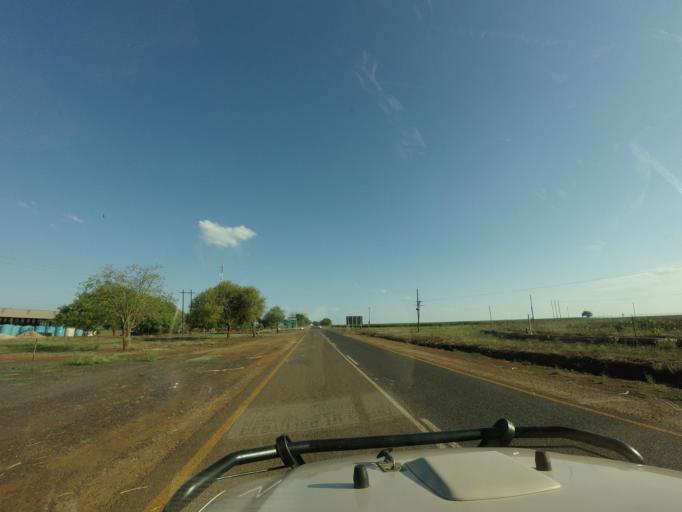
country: ZA
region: Mpumalanga
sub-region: Ehlanzeni District
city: Komatipoort
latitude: -25.3904
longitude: 31.9139
